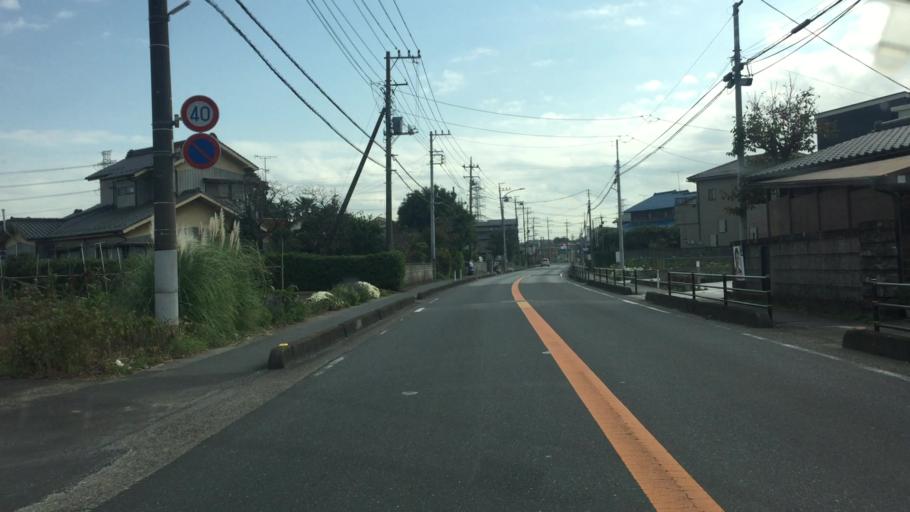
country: JP
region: Saitama
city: Yoshikawa
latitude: 35.8764
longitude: 139.8597
